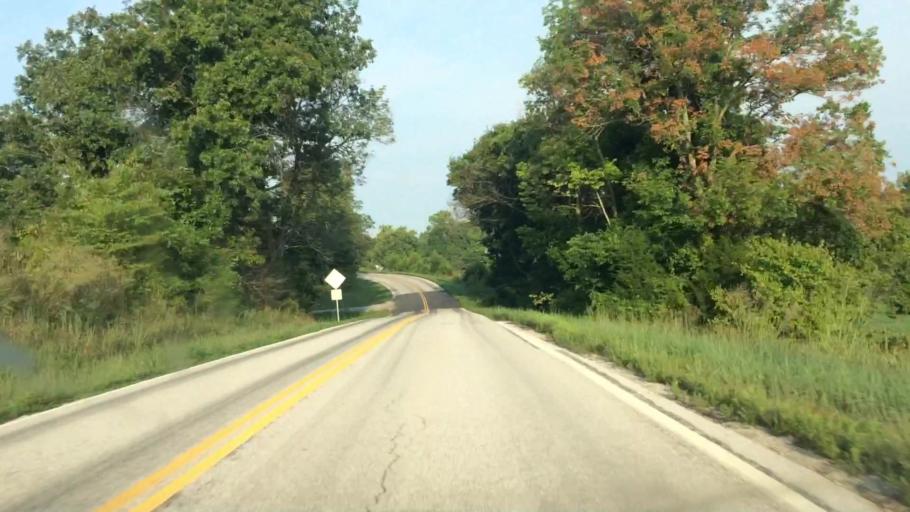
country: US
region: Missouri
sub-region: Greene County
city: Strafford
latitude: 37.1908
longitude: -93.1083
